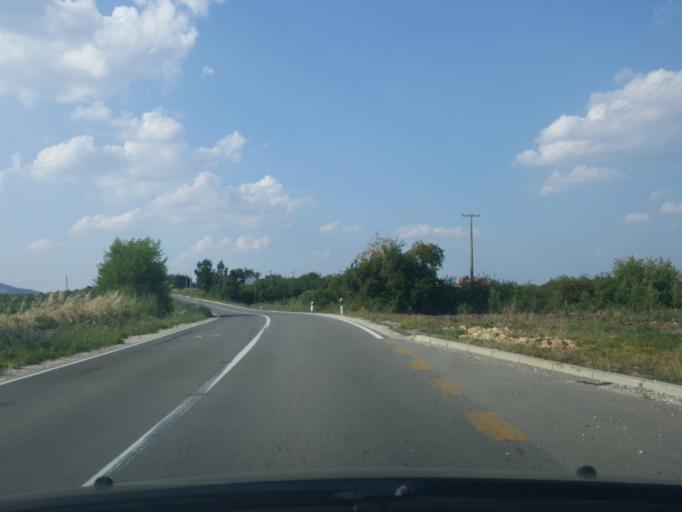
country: RS
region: Central Serbia
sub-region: Sumadijski Okrug
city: Topola
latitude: 44.2119
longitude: 20.6193
